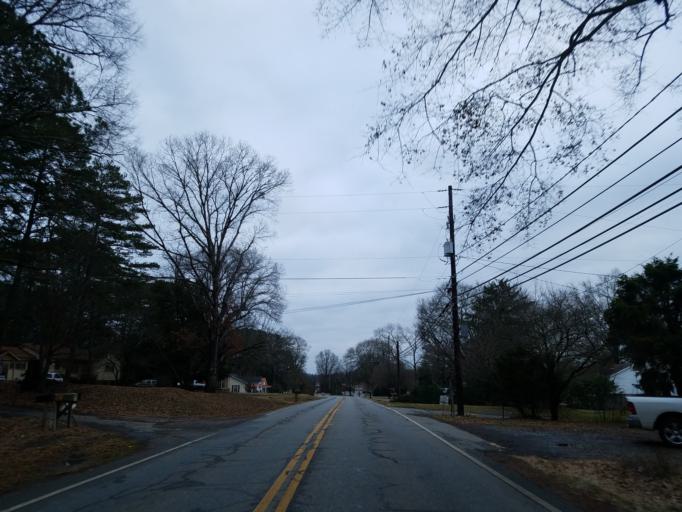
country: US
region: Georgia
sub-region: Bartow County
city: Cartersville
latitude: 34.1935
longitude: -84.8226
